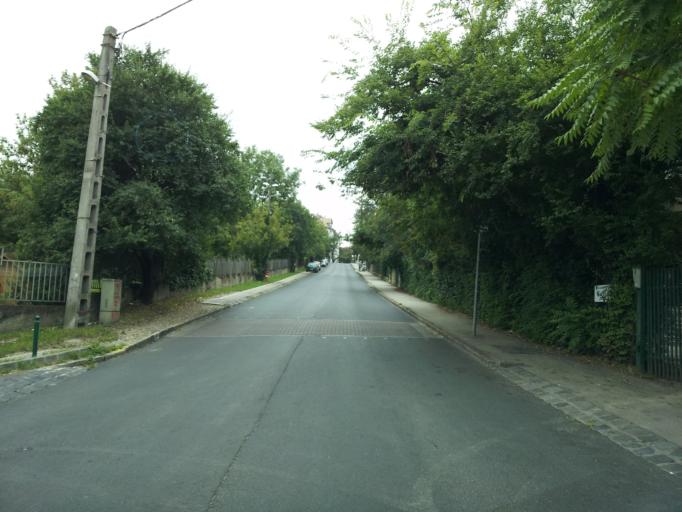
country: HU
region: Budapest
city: Budapest II. keruelet
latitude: 47.5135
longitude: 19.0206
